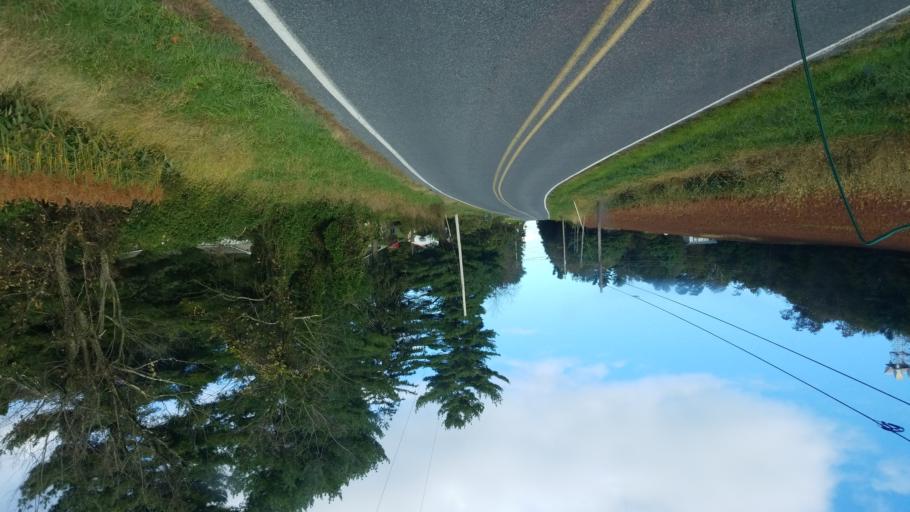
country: US
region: Pennsylvania
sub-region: Franklin County
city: Fayetteville
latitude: 39.8973
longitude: -77.4193
